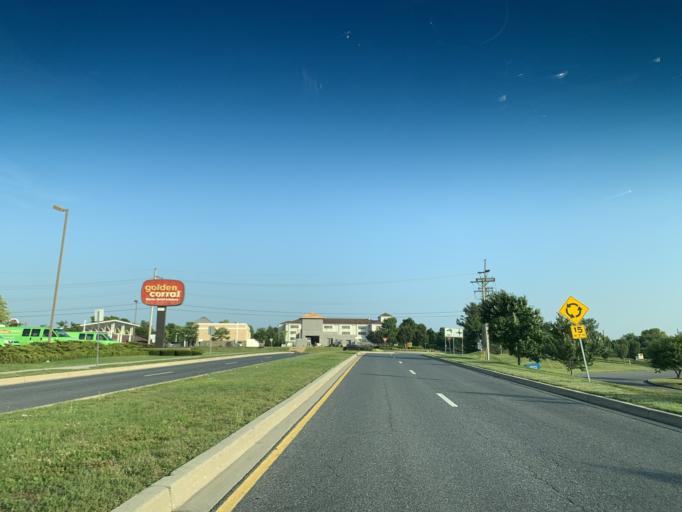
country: US
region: Maryland
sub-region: Frederick County
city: Frederick
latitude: 39.3828
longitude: -77.4024
